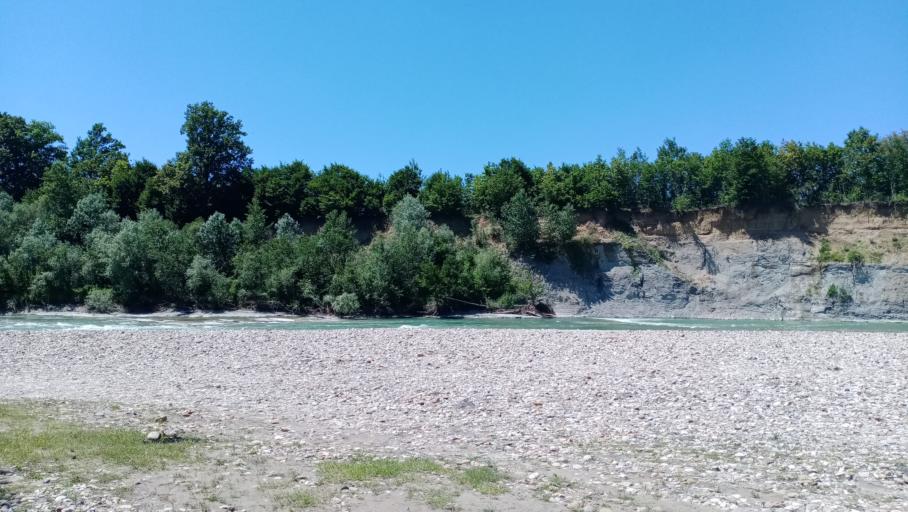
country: RU
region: Krasnodarskiy
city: Neftegorsk
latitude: 44.3774
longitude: 39.7979
